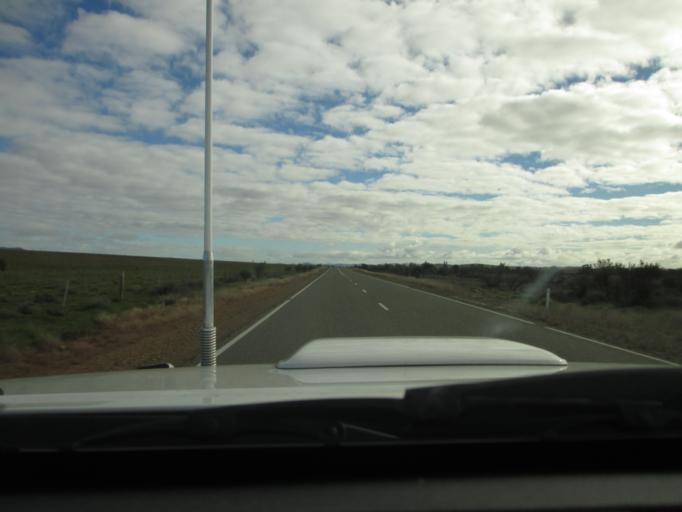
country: AU
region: South Australia
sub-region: Flinders Ranges
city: Quorn
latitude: -32.4046
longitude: 138.5169
